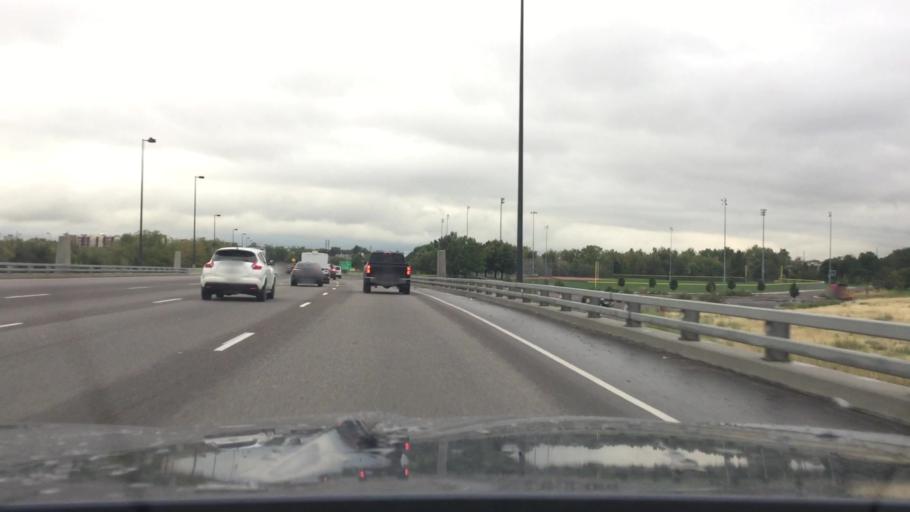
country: US
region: Colorado
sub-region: Denver County
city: Denver
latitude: 39.7035
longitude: -104.9962
